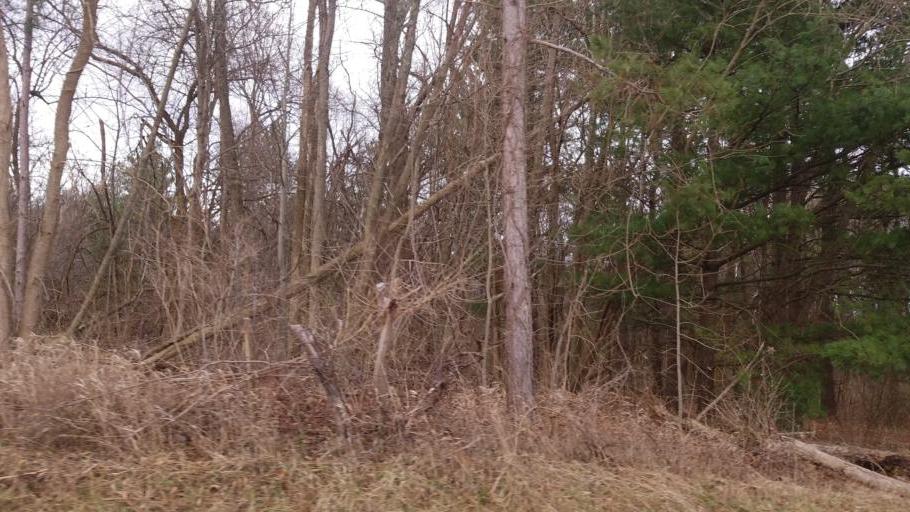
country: US
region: Ohio
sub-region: Knox County
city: Centerburg
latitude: 40.3682
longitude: -82.6198
